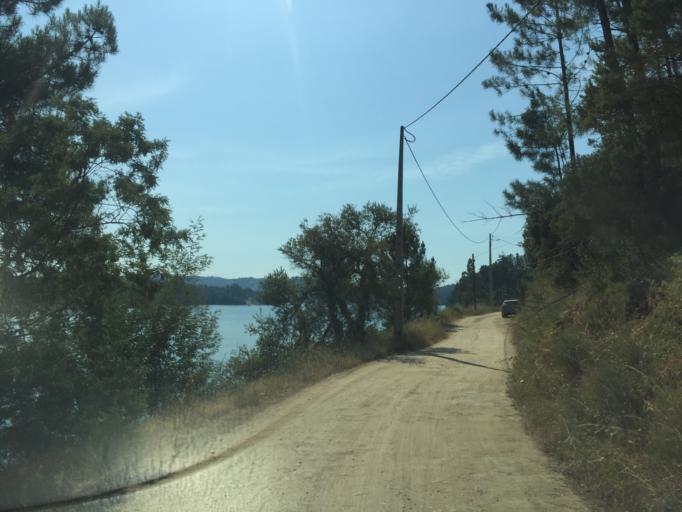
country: PT
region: Santarem
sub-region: Ferreira do Zezere
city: Ferreira do Zezere
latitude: 39.6077
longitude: -8.2772
